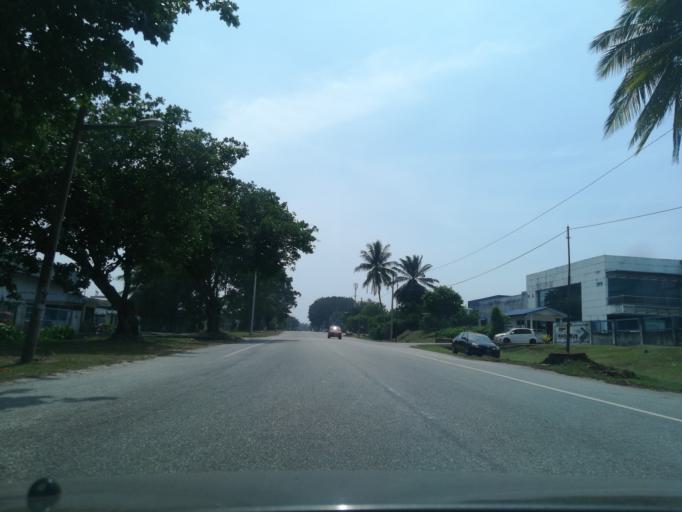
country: MY
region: Kedah
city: Kulim
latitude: 5.4115
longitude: 100.5621
